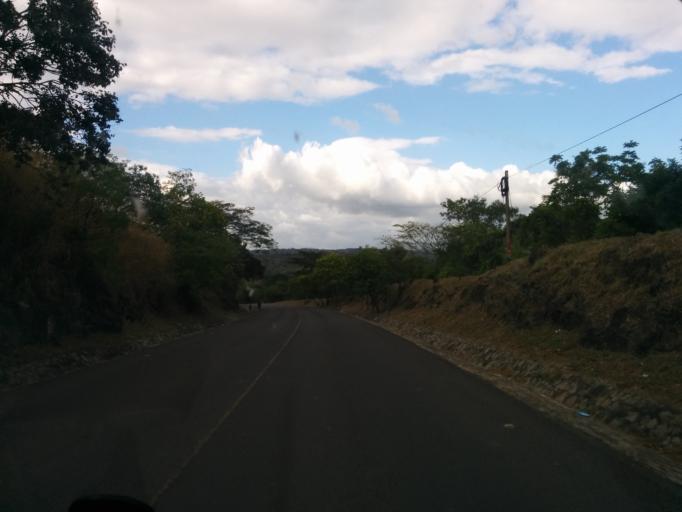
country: NI
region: Esteli
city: Esteli
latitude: 13.1734
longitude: -86.3664
